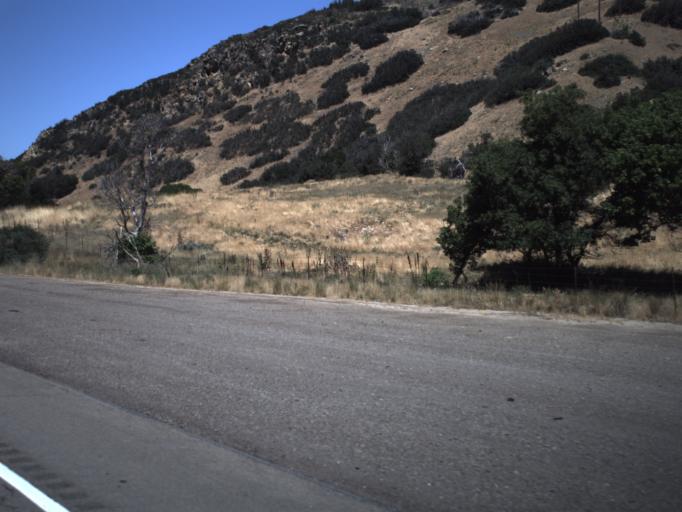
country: US
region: Utah
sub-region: Utah County
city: Mapleton
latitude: 40.0356
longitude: -111.5259
